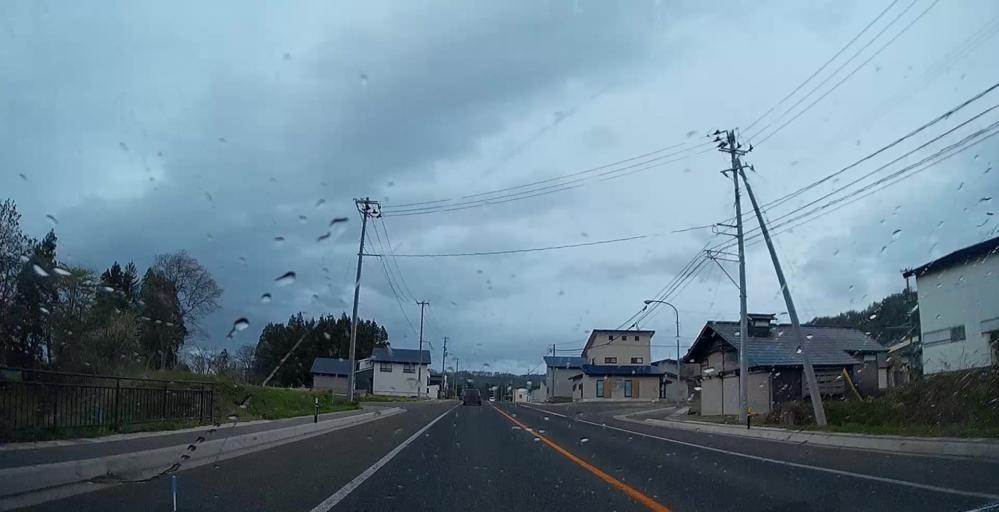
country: JP
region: Yamagata
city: Nagai
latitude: 38.0140
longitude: 139.9693
